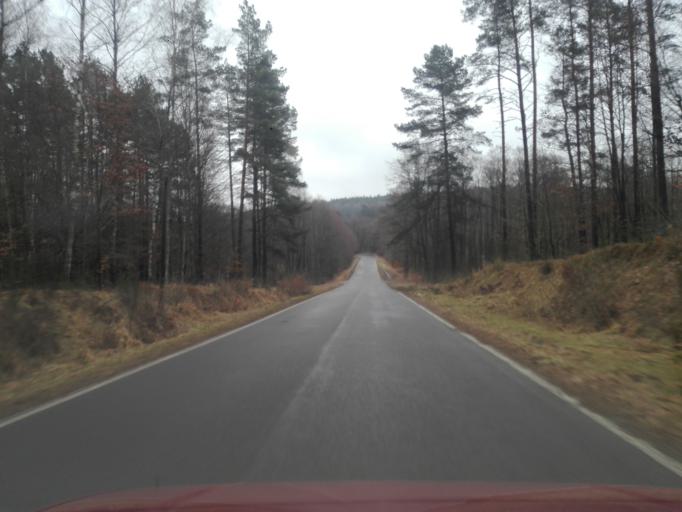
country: PL
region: West Pomeranian Voivodeship
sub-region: Powiat koszalinski
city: Polanow
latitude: 54.1510
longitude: 16.6884
